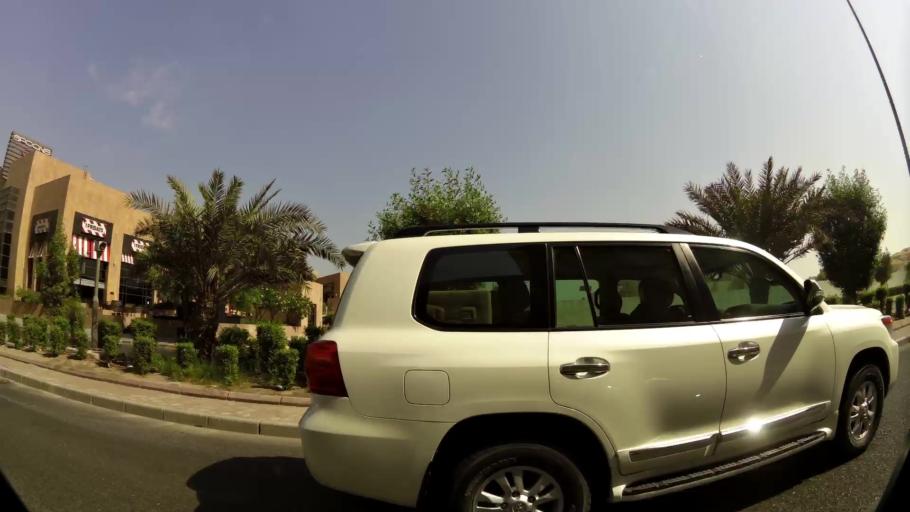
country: KW
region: Al Ahmadi
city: Al Mahbulah
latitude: 29.1534
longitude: 48.1248
